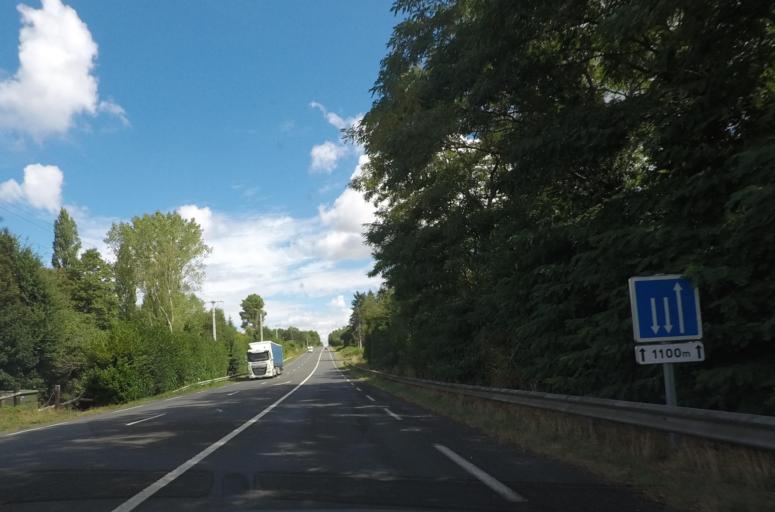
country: FR
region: Pays de la Loire
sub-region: Departement de la Sarthe
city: Cerans-Foulletourte
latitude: 47.8049
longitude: 0.0546
